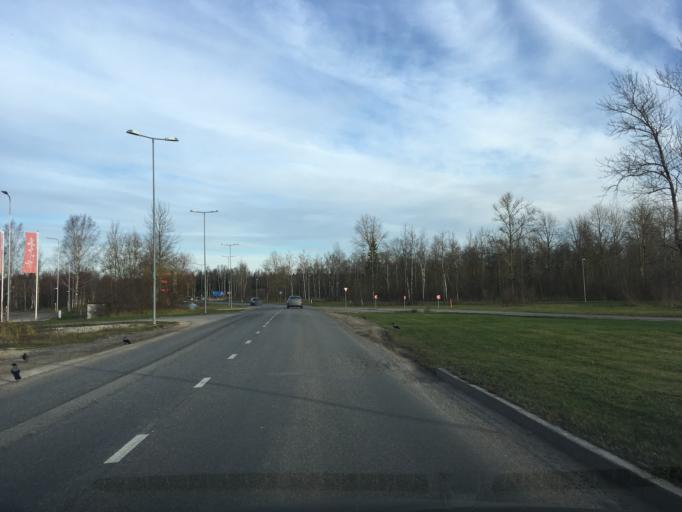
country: EE
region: Ida-Virumaa
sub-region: Johvi vald
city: Johvi
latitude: 59.3658
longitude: 27.4165
